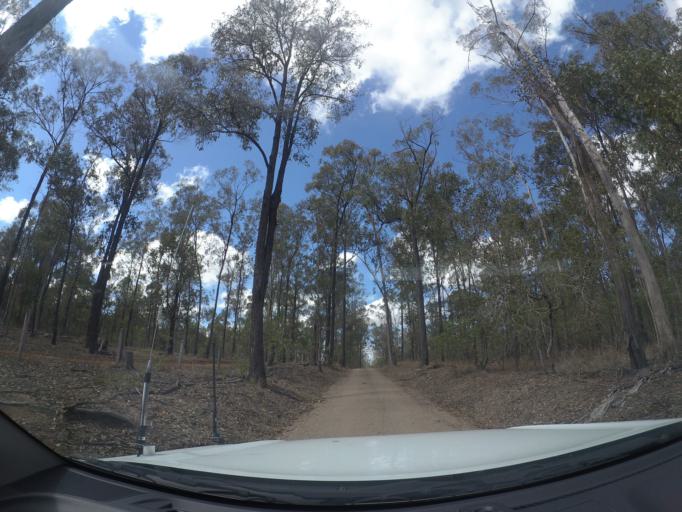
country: AU
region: Queensland
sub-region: Logan
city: North Maclean
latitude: -27.8247
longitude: 152.9690
